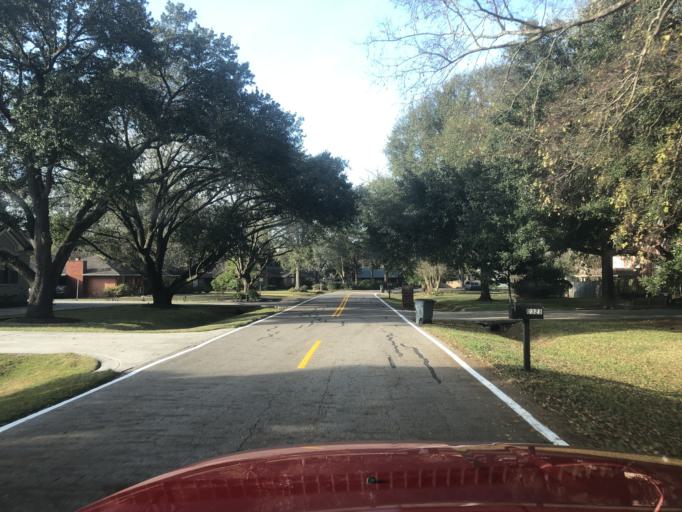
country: US
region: Texas
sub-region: Harris County
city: Spring
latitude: 30.0143
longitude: -95.4717
